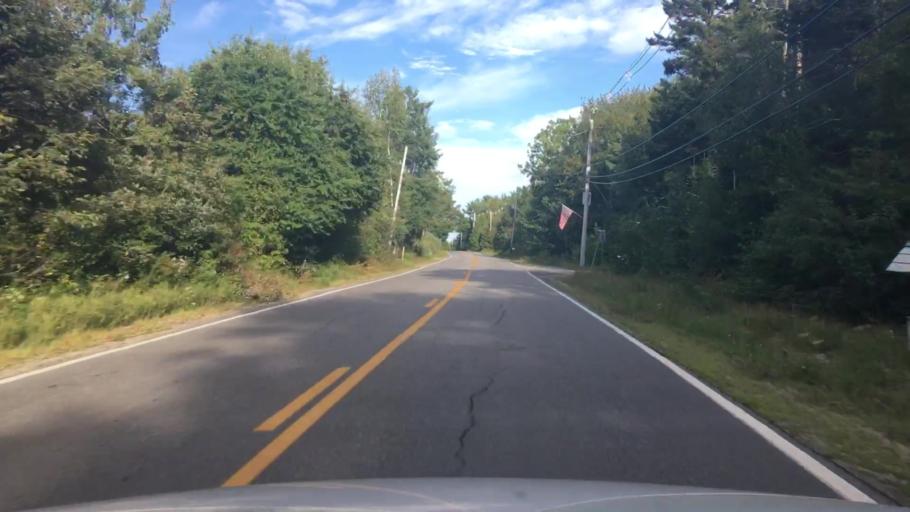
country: US
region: Maine
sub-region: Hancock County
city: Trenton
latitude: 44.4374
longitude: -68.3834
